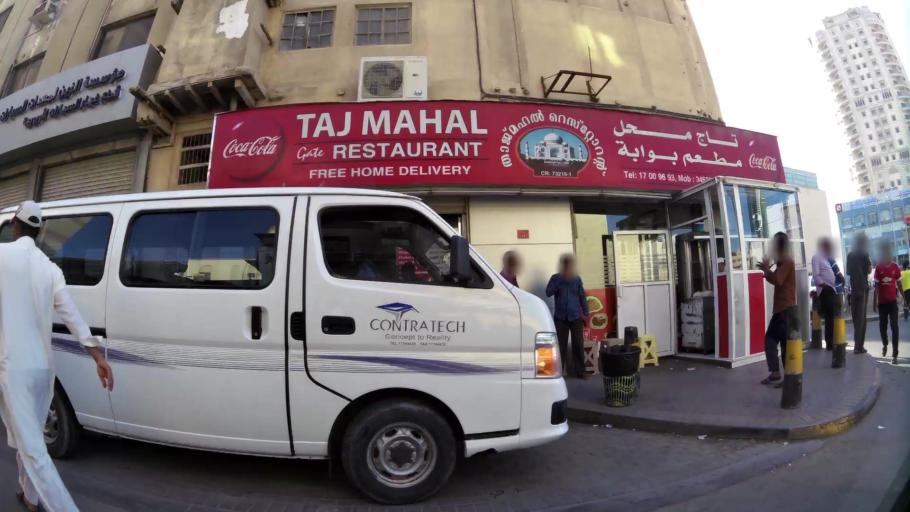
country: BH
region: Manama
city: Manama
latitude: 26.2299
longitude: 50.5711
